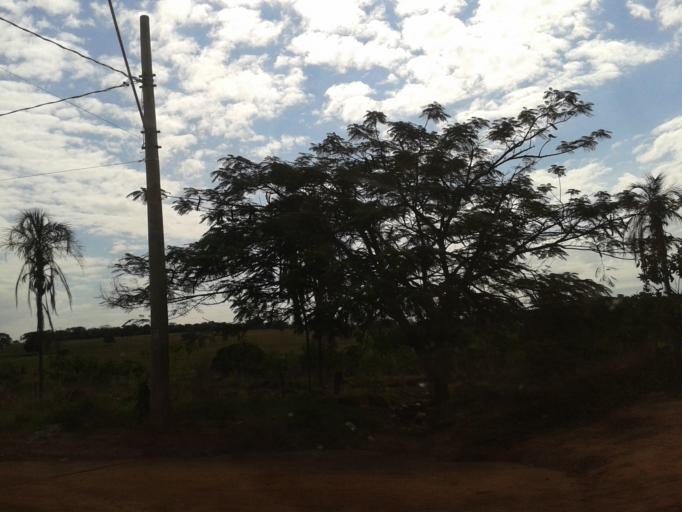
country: BR
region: Minas Gerais
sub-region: Santa Vitoria
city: Santa Vitoria
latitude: -18.8350
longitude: -50.1161
